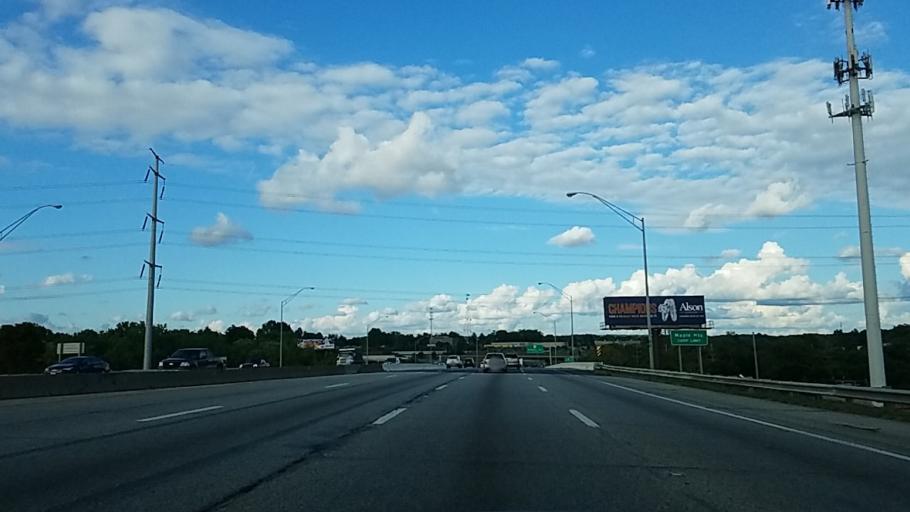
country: US
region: Ohio
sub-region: Cuyahoga County
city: Maple Heights
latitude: 41.4221
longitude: -81.5851
